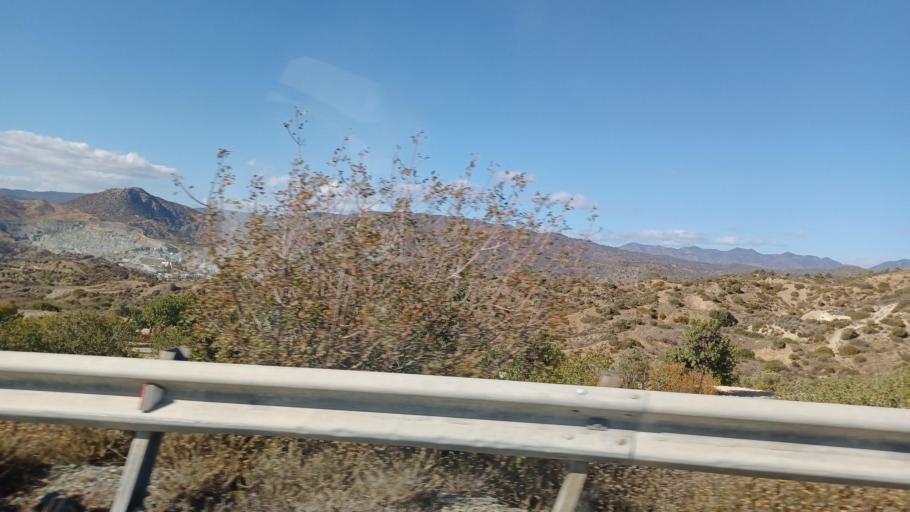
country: CY
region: Limassol
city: Pyrgos
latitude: 34.7687
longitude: 33.2372
